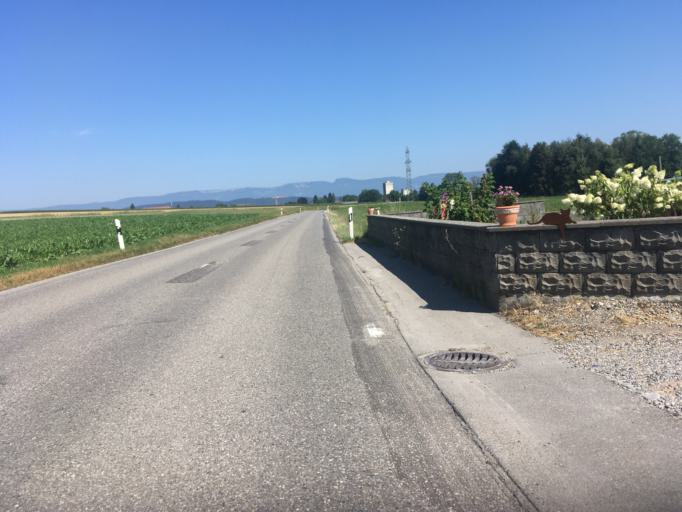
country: CH
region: Bern
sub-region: Bern-Mittelland District
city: Fraubrunnen
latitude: 47.0772
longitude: 7.5308
